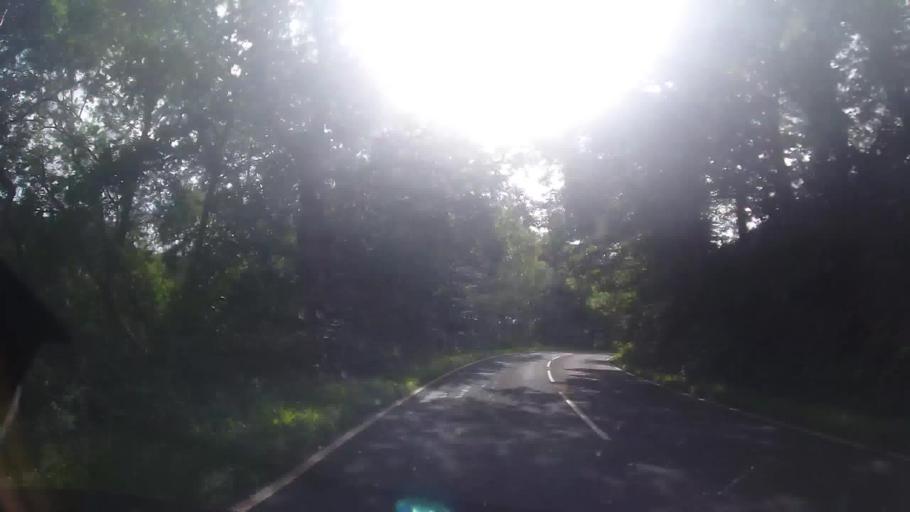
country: GB
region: Wales
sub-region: Gwynedd
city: Barmouth
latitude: 52.7401
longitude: -4.0096
